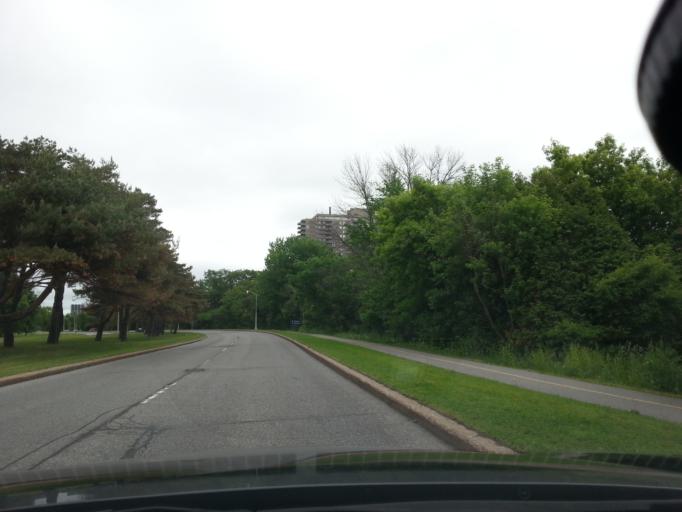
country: CA
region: Ontario
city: Ottawa
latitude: 45.4005
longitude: -75.7567
